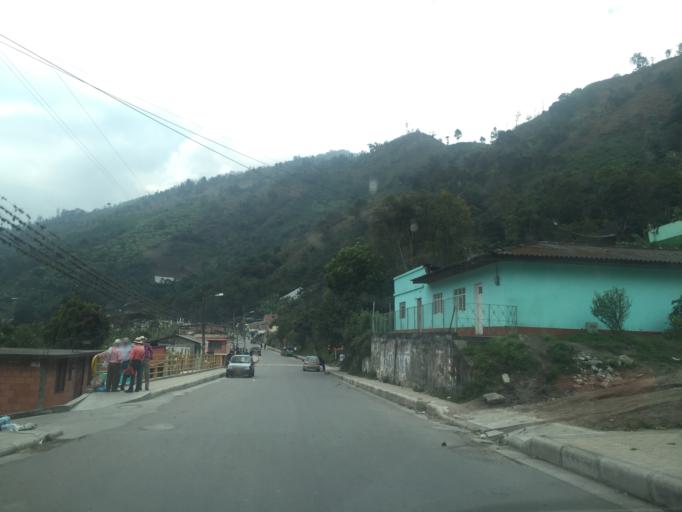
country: CO
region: Tolima
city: Cajamarca
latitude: 4.4370
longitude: -75.4309
